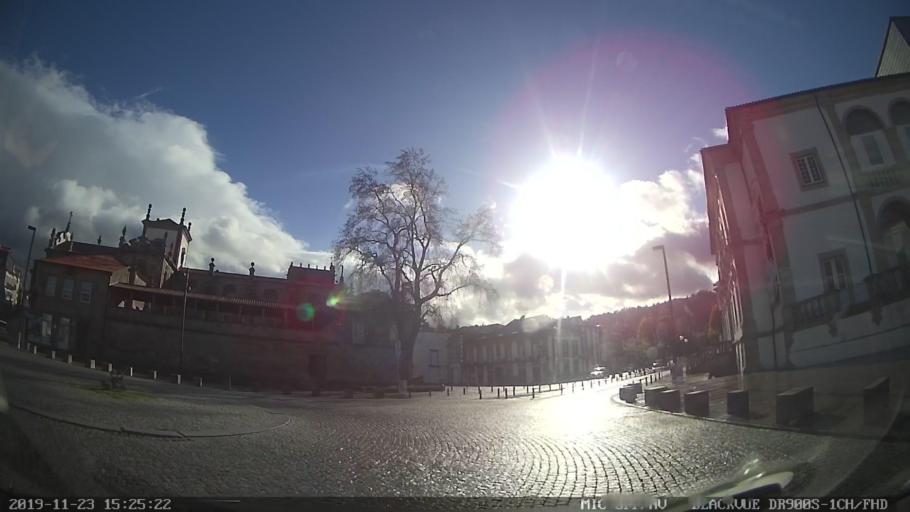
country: PT
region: Viseu
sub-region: Lamego
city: Lamego
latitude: 41.0976
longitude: -7.8070
